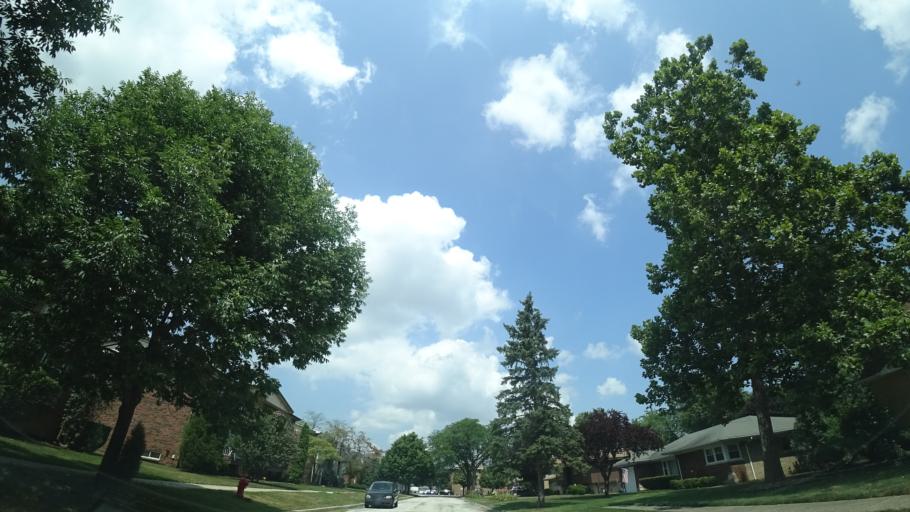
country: US
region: Illinois
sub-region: Cook County
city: Worth
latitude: 41.6944
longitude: -87.7965
